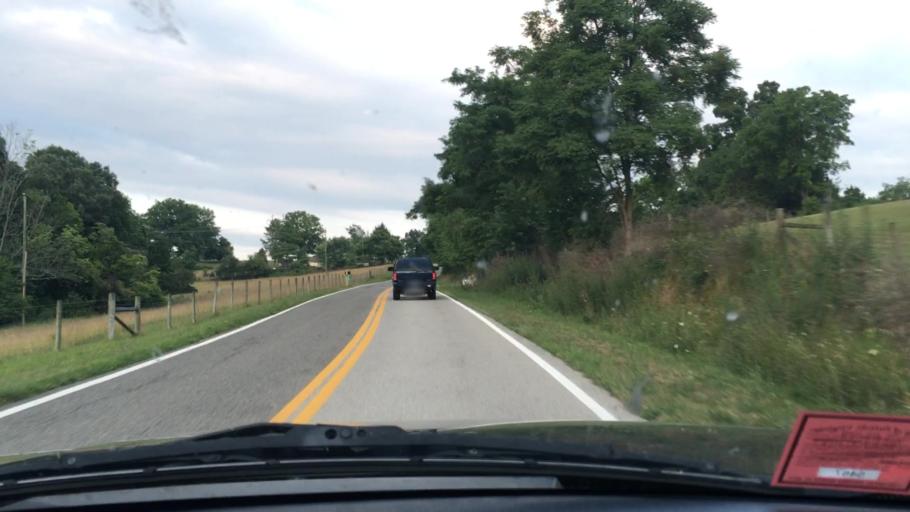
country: US
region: Virginia
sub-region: Pulaski County
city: Dublin
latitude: 37.0574
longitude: -80.7020
